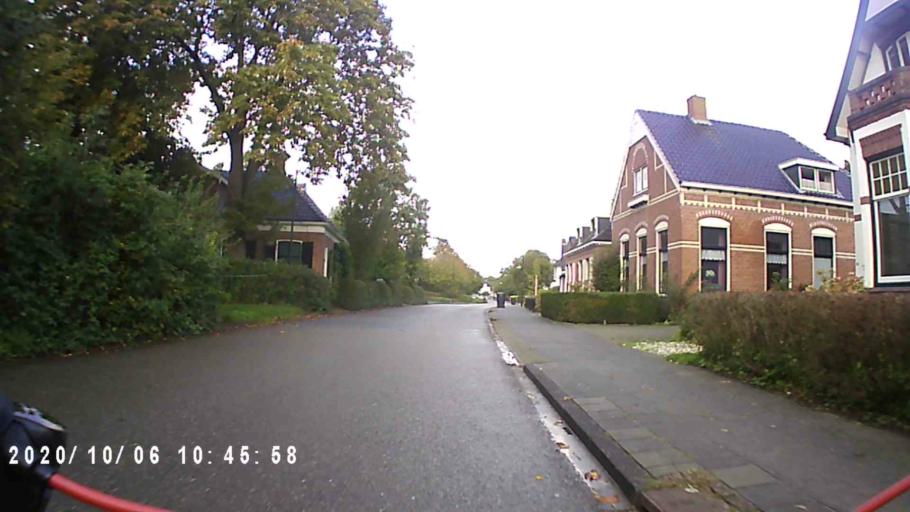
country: NL
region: Groningen
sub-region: Gemeente Zuidhorn
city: Oldehove
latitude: 53.3598
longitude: 6.4220
